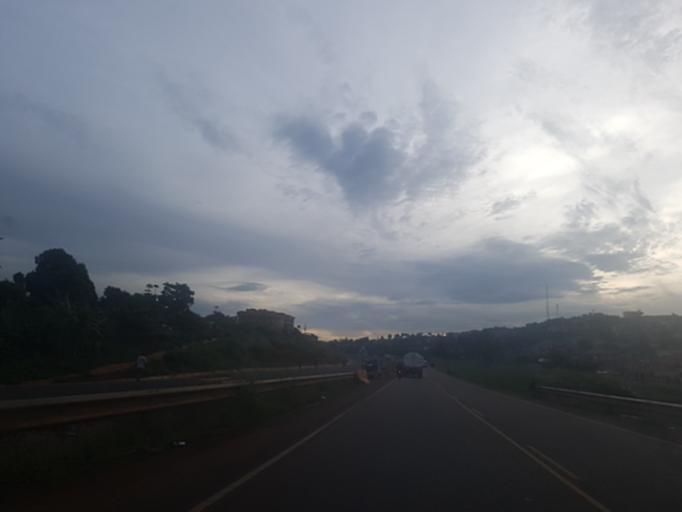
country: UG
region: Central Region
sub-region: Wakiso District
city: Kireka
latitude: 0.3689
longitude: 32.6181
